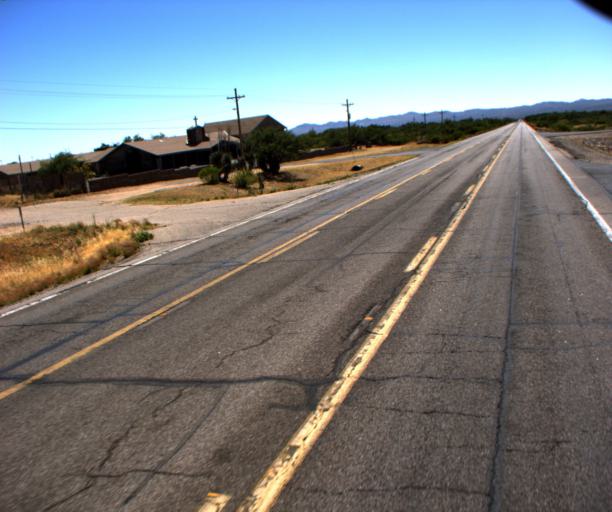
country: US
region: Arizona
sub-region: Pinal County
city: Oracle
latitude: 32.6178
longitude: -110.8155
